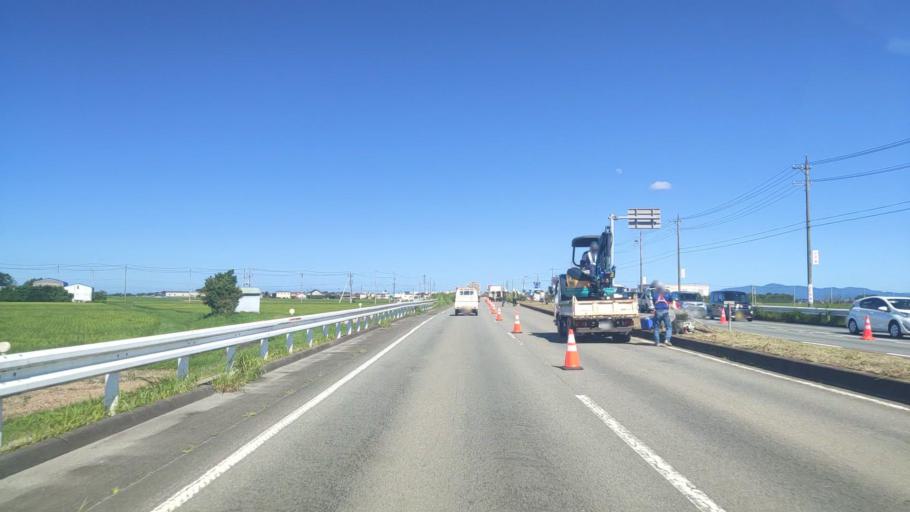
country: JP
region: Mie
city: Ise
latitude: 34.5858
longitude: 136.6047
